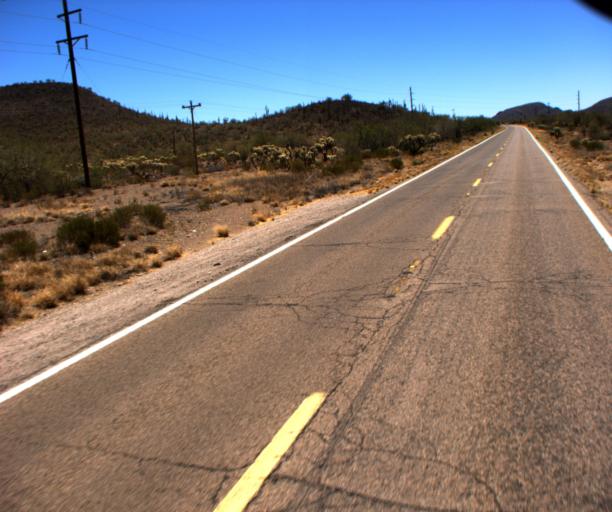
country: US
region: Arizona
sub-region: Pima County
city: Sells
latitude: 31.9877
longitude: -111.9754
